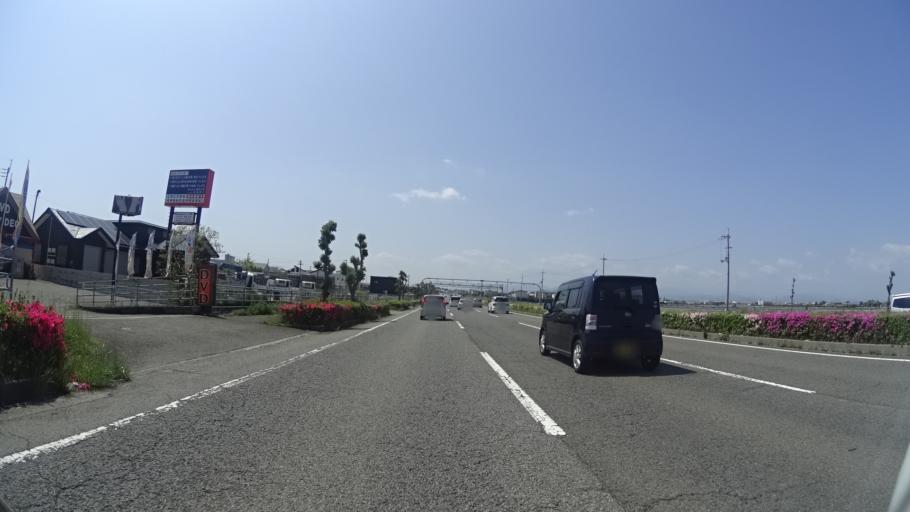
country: JP
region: Tokushima
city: Narutocho-mitsuishi
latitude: 34.1531
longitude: 134.5796
